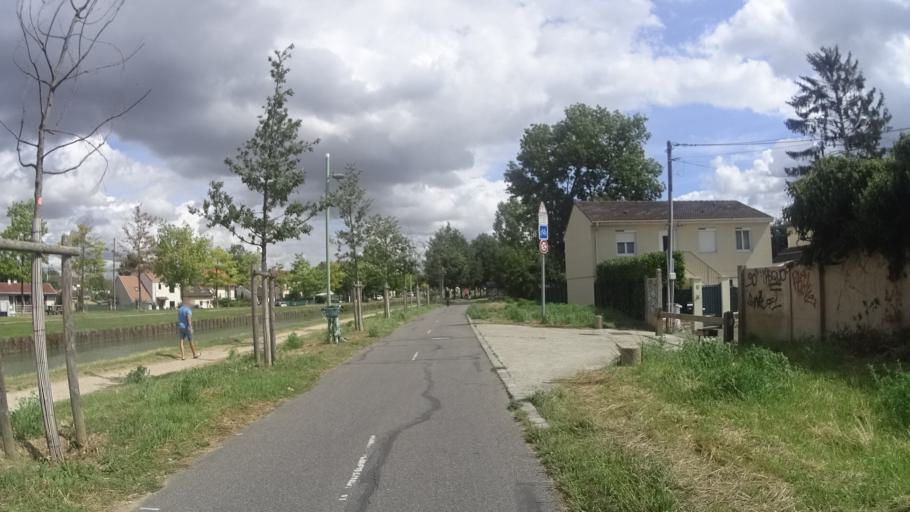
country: FR
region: Ile-de-France
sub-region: Departement de Seine-Saint-Denis
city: Sevran
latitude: 48.9312
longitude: 2.5208
